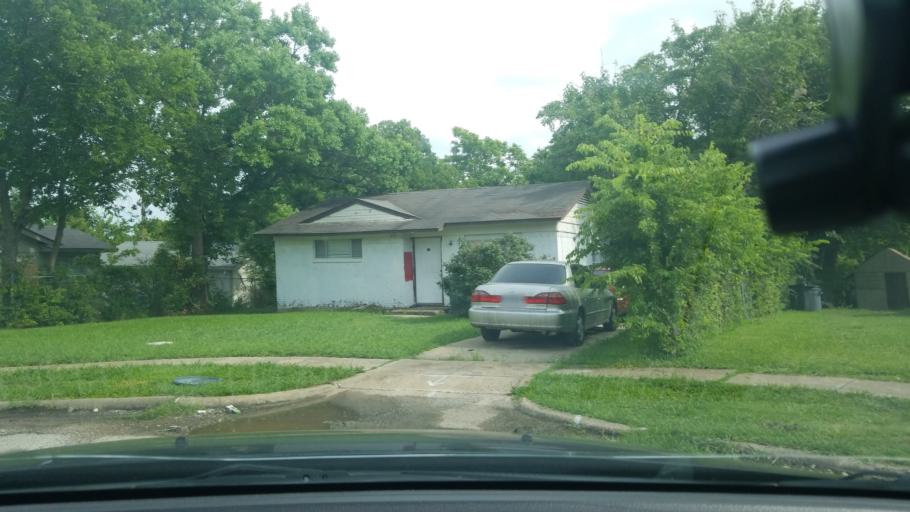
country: US
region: Texas
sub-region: Dallas County
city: Mesquite
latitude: 32.7591
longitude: -96.6240
